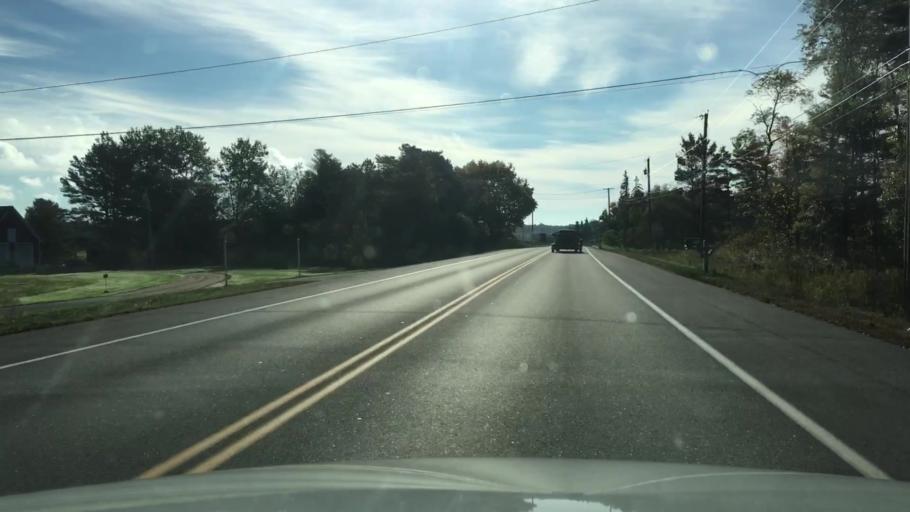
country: US
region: Maine
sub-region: Knox County
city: Warren
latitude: 44.0857
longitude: -69.2304
